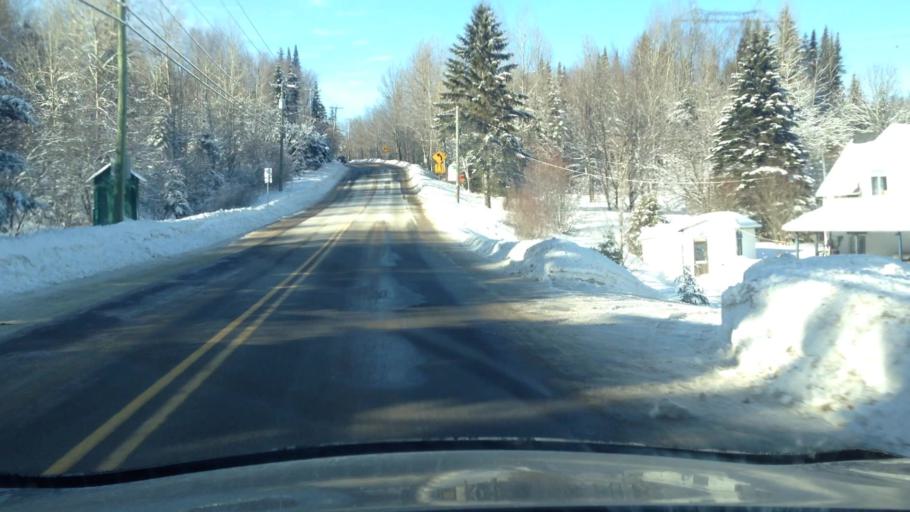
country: CA
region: Quebec
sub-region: Laurentides
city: Sainte-Agathe-des-Monts
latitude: 45.9334
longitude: -74.4341
